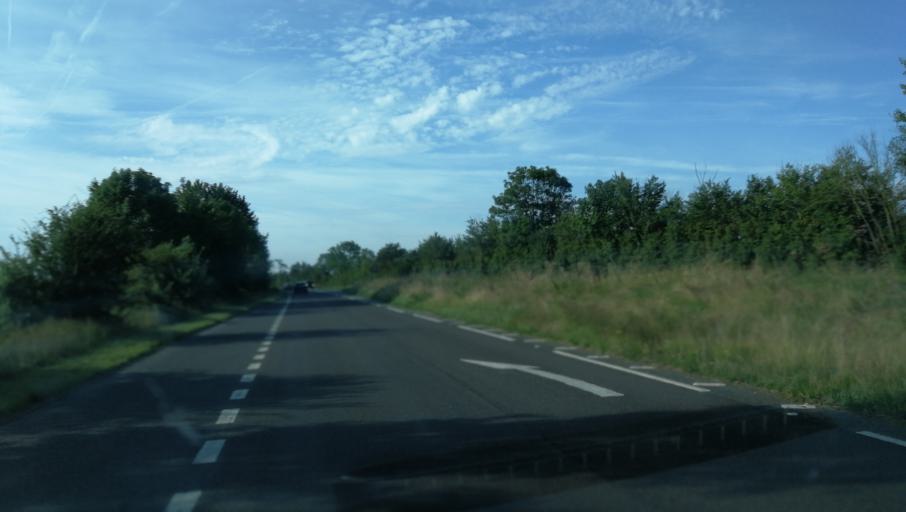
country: GB
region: England
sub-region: Oxfordshire
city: Deddington
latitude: 51.9383
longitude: -1.3265
